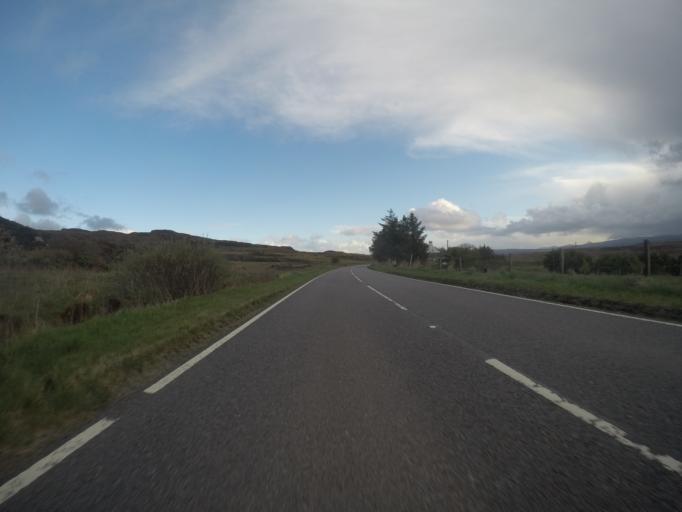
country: GB
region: Scotland
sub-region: Highland
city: Portree
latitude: 57.5604
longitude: -6.3635
